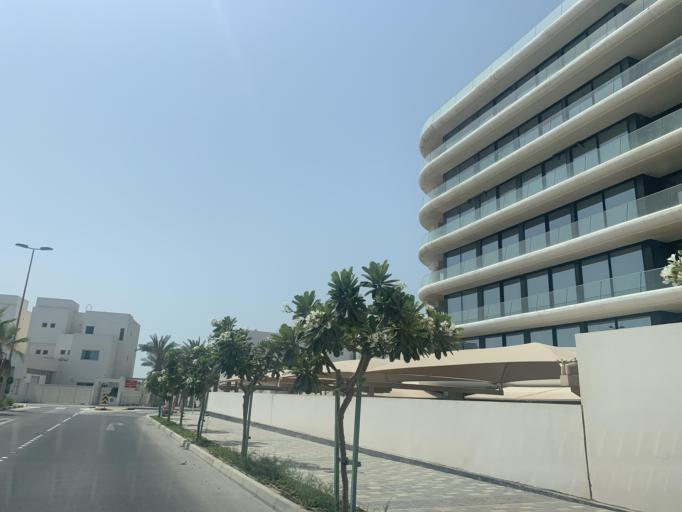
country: BH
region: Muharraq
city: Al Hadd
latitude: 26.2745
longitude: 50.6721
